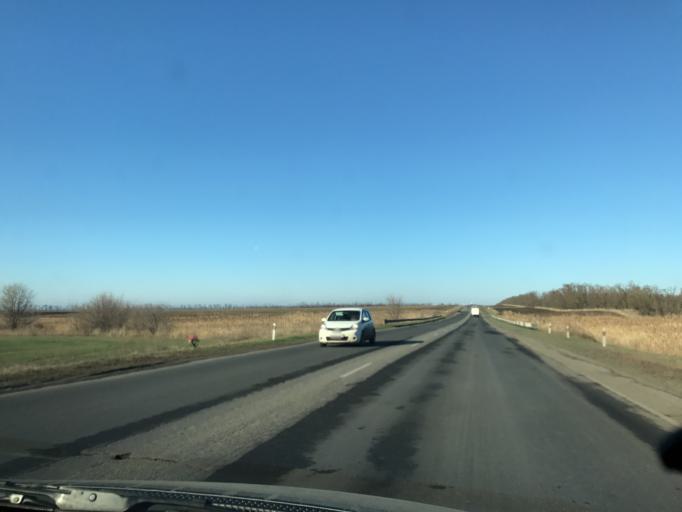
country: RU
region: Rostov
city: Kagal'nitskaya
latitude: 46.8563
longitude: 40.1937
